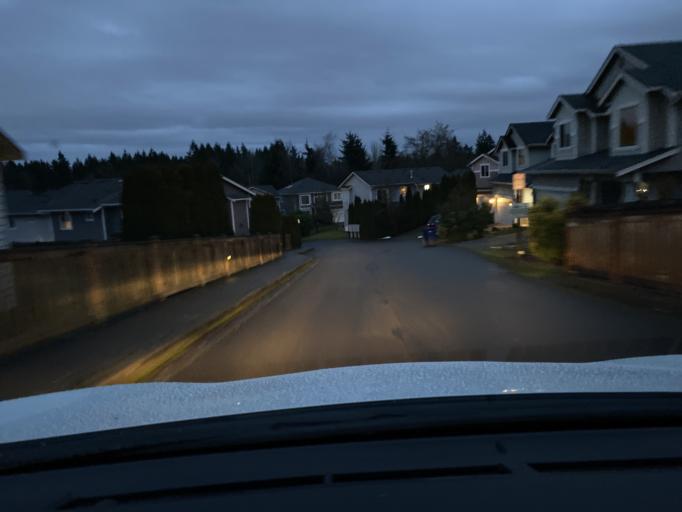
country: US
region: Washington
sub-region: Snohomish County
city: Martha Lake
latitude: 47.8705
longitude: -122.2703
